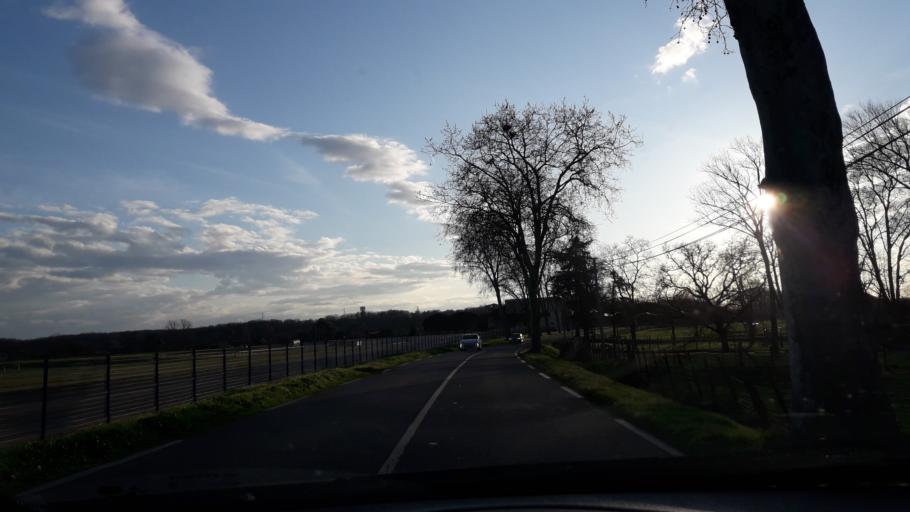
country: FR
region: Midi-Pyrenees
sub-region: Departement de la Haute-Garonne
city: Grenade
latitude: 43.7542
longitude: 1.2830
